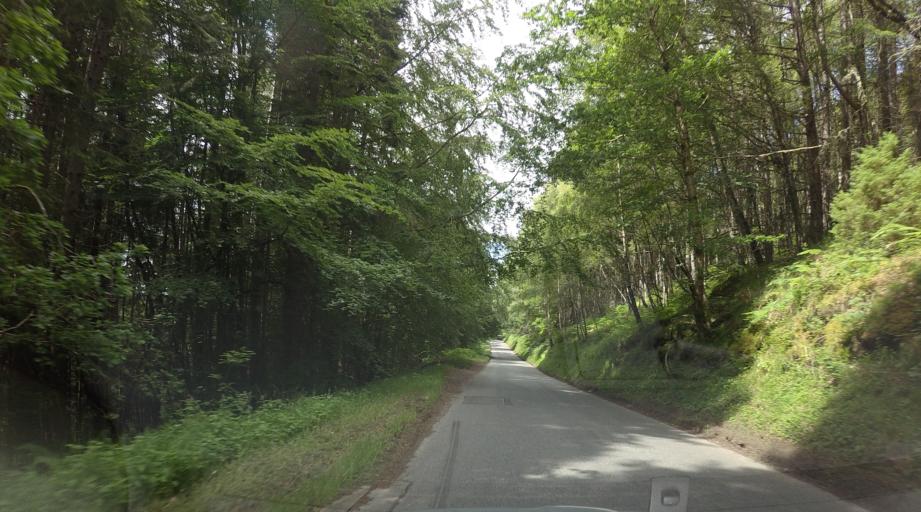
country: GB
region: Scotland
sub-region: Perth and Kinross
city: Aberfeldy
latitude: 56.7185
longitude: -3.8814
